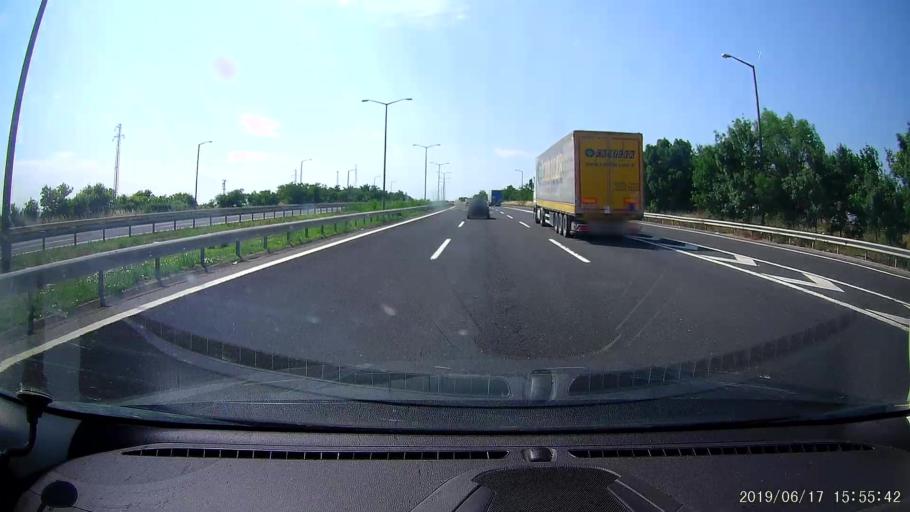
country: TR
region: Istanbul
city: Buyukcavuslu
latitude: 41.2055
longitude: 28.0071
